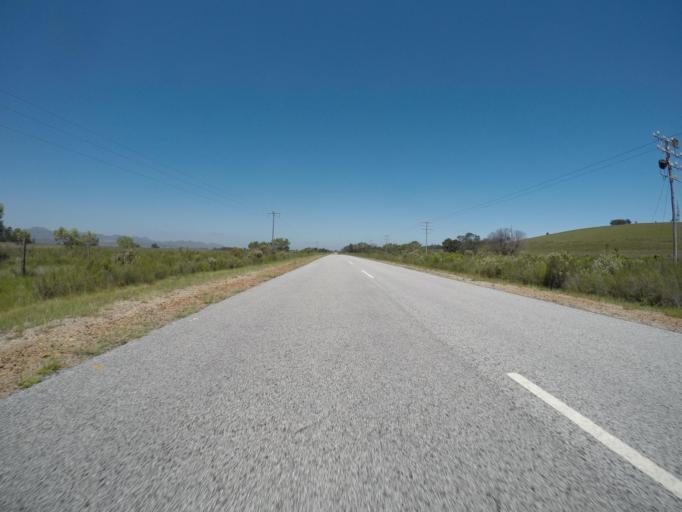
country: ZA
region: Eastern Cape
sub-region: Cacadu District Municipality
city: Kruisfontein
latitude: -33.9831
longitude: 24.5112
